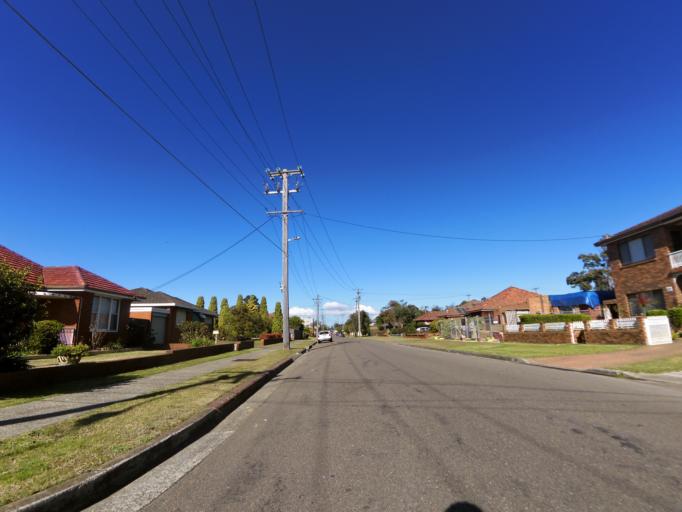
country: AU
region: New South Wales
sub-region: Rockdale
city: Banksia
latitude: -33.9514
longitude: 151.1536
